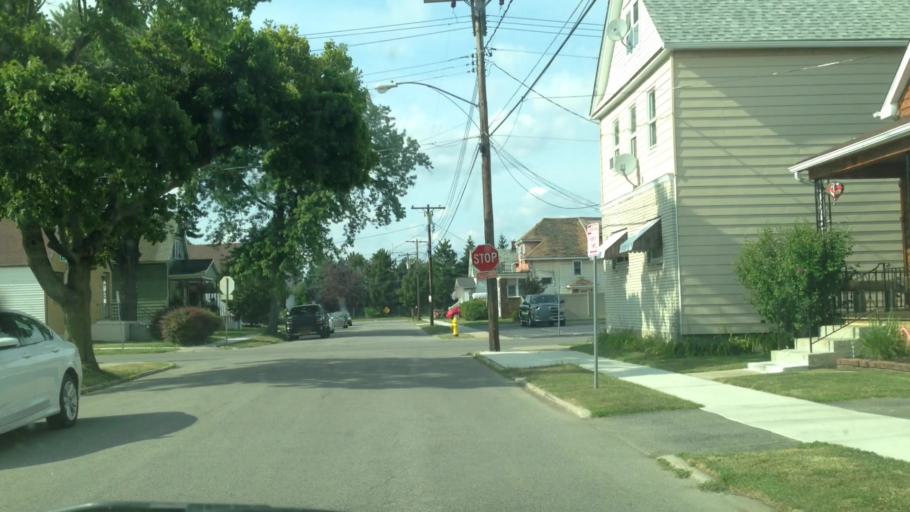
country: US
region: New York
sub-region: Erie County
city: Sloan
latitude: 42.8744
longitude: -78.7978
